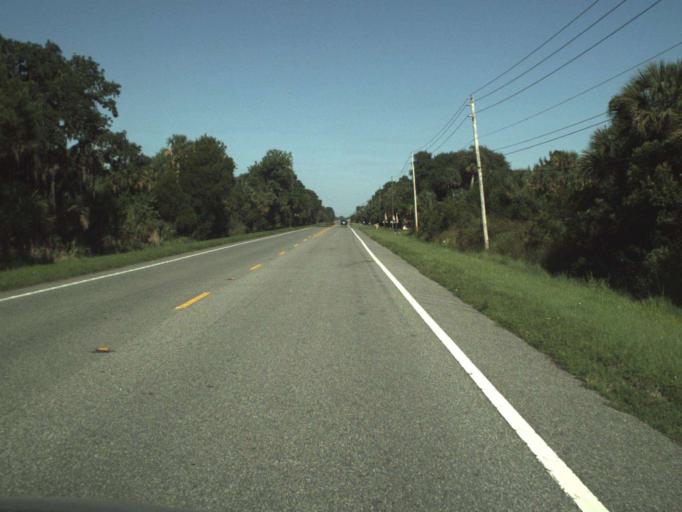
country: US
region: Florida
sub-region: Seminole County
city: Geneva
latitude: 28.7174
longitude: -81.0639
